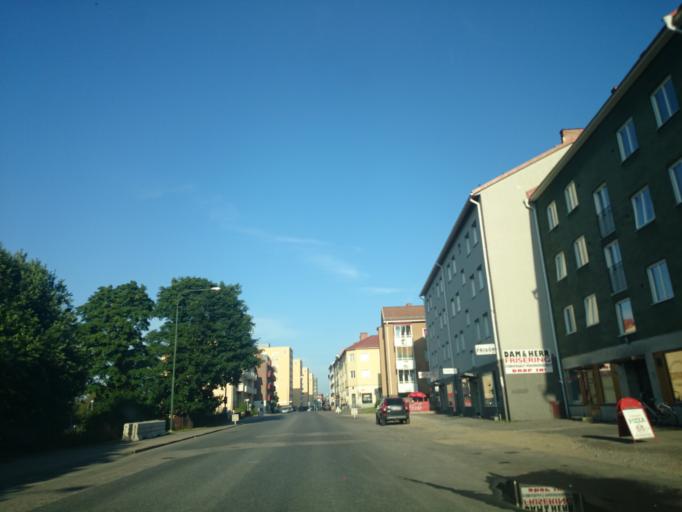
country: SE
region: Vaesternorrland
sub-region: Sundsvalls Kommun
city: Sundsvall
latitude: 62.3929
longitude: 17.2865
